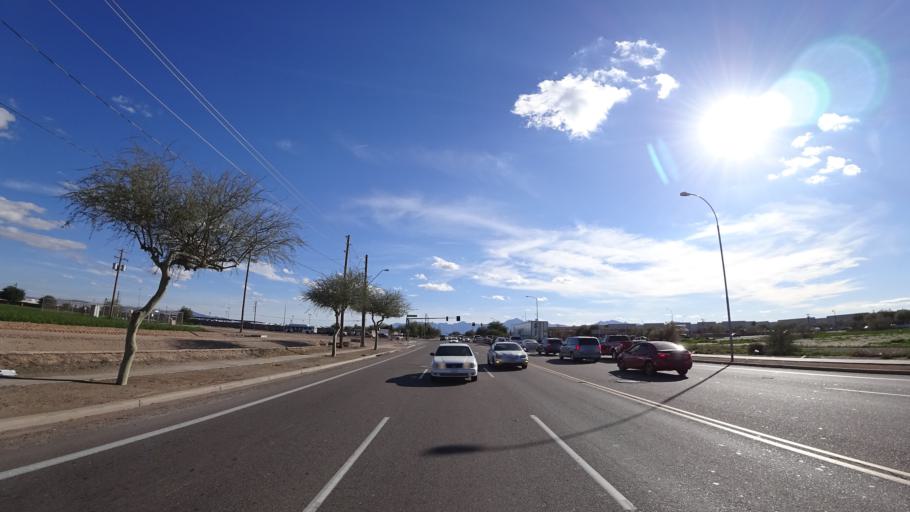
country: US
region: Arizona
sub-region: Maricopa County
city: Tolleson
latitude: 33.4528
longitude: -112.2383
